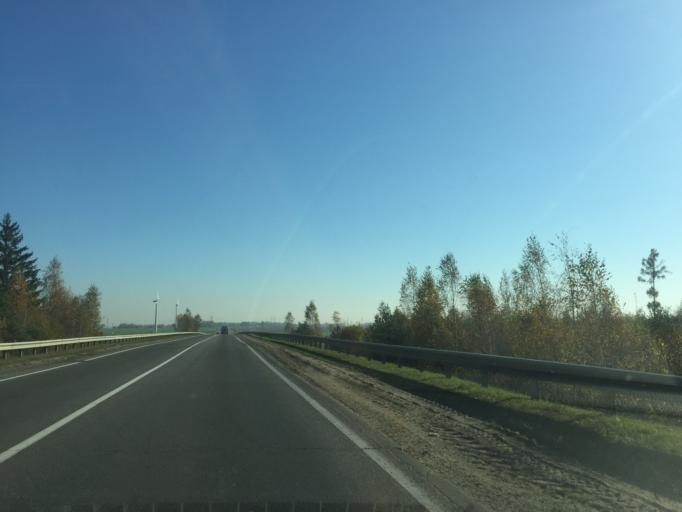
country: BY
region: Mogilev
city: Palykavichy Pyershyya
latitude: 53.9802
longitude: 30.3261
